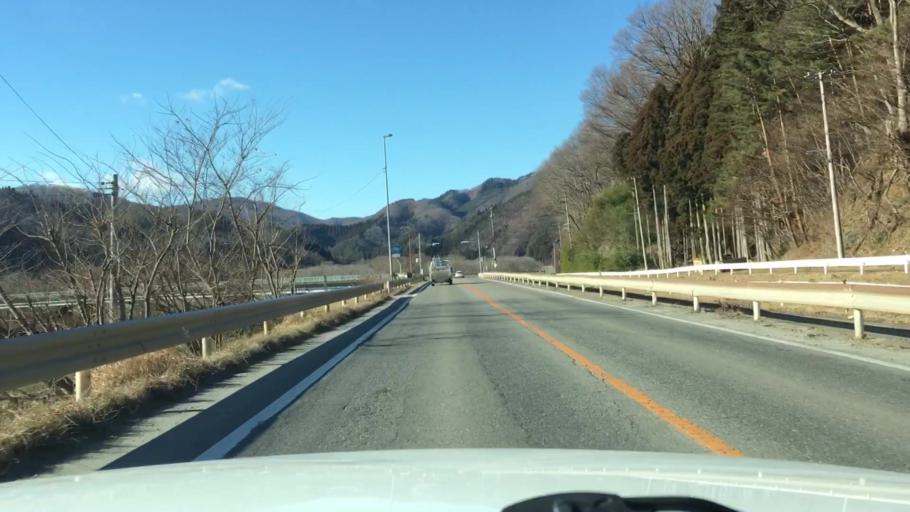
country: JP
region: Iwate
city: Miyako
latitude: 39.6293
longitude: 141.8568
